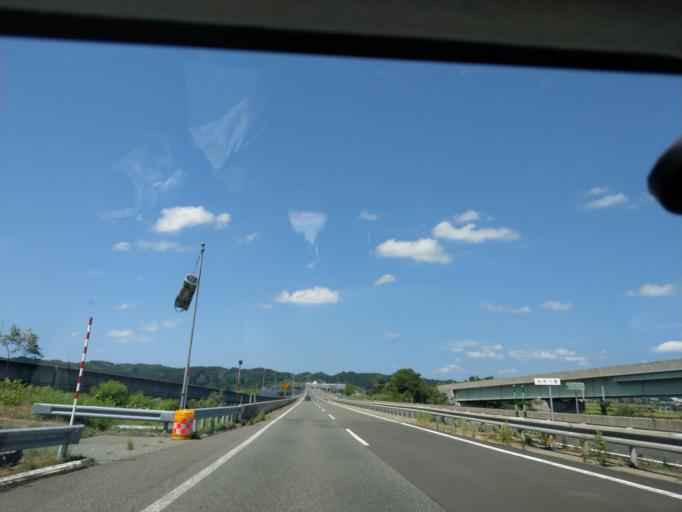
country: JP
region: Akita
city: Akita
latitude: 39.6412
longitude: 140.2107
